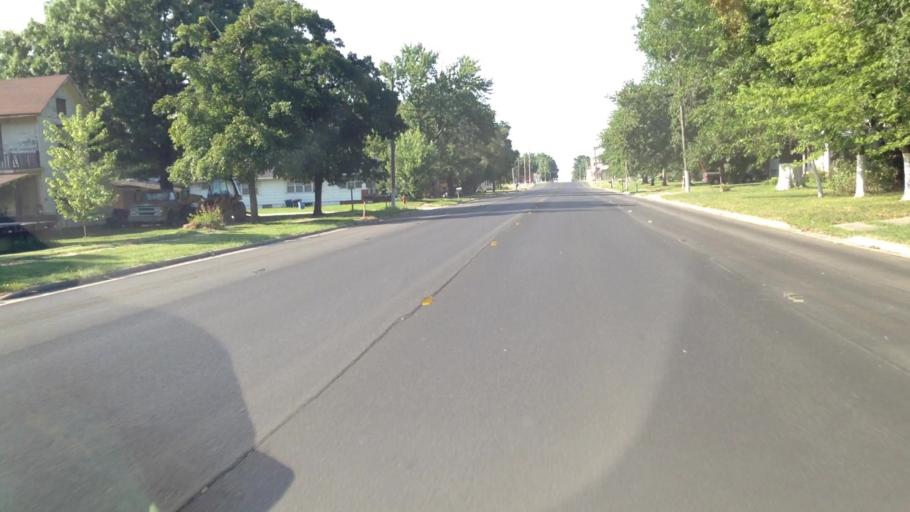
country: US
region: Kansas
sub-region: Allen County
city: Iola
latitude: 37.9116
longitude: -95.1701
